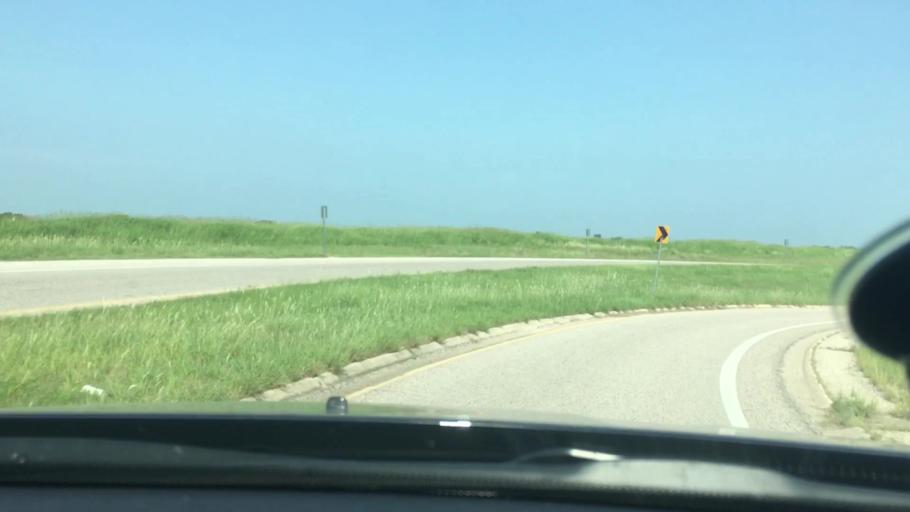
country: US
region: Oklahoma
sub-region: Pontotoc County
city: Ada
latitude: 34.7254
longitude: -96.6361
